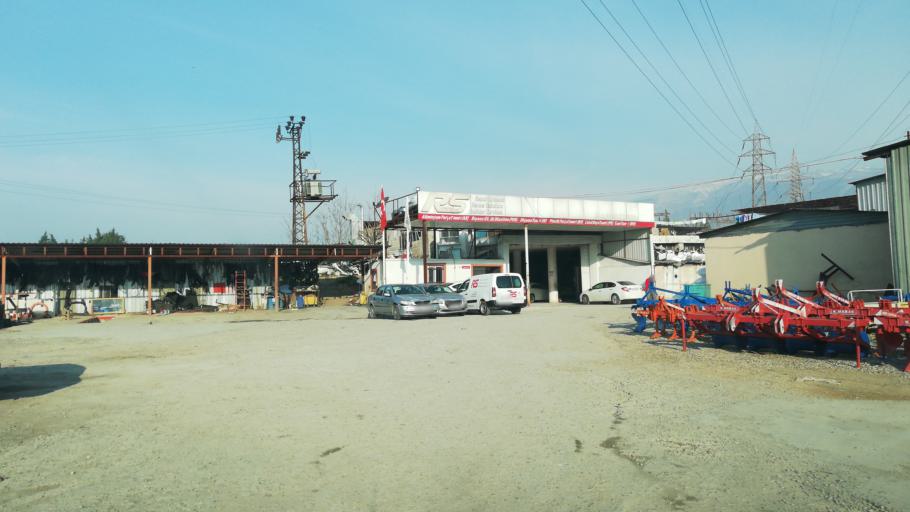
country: TR
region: Kahramanmaras
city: Kahramanmaras
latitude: 37.5645
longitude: 36.9450
